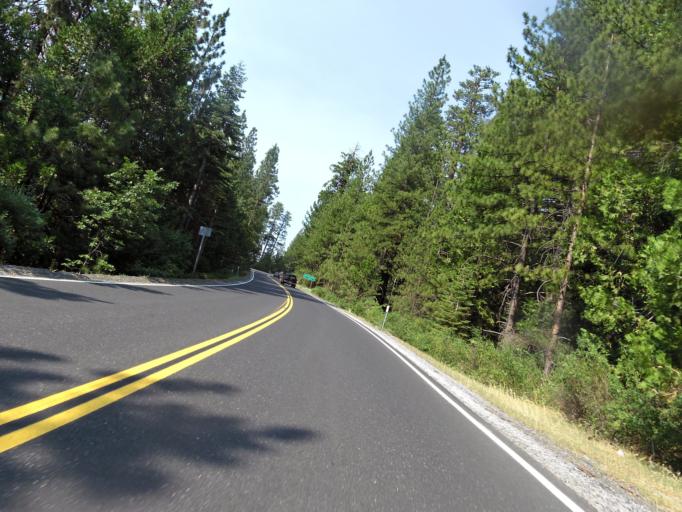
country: US
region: California
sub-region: Tuolumne County
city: Twain Harte
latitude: 38.1496
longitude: -120.0718
